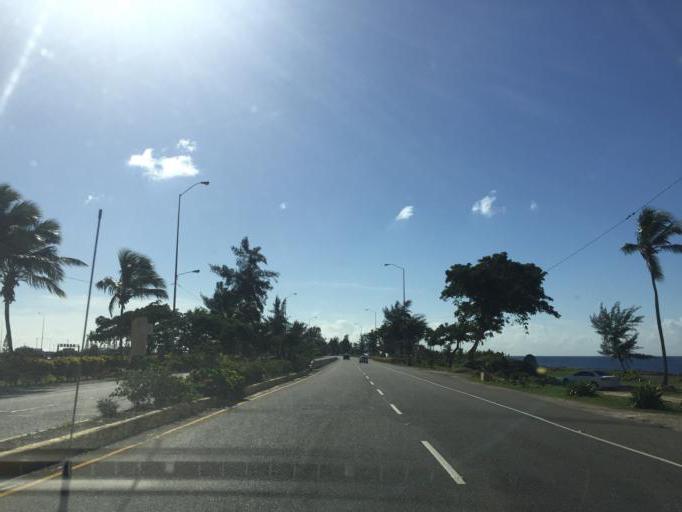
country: DO
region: Santo Domingo
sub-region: Santo Domingo
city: Boca Chica
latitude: 18.4336
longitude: -69.6806
